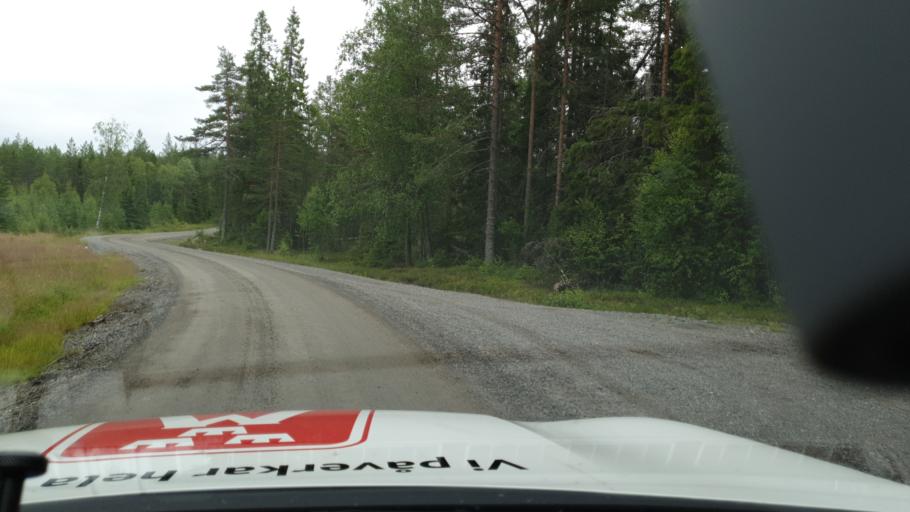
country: SE
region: Vaesterbotten
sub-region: Robertsfors Kommun
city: Robertsfors
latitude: 64.0262
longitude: 20.8884
